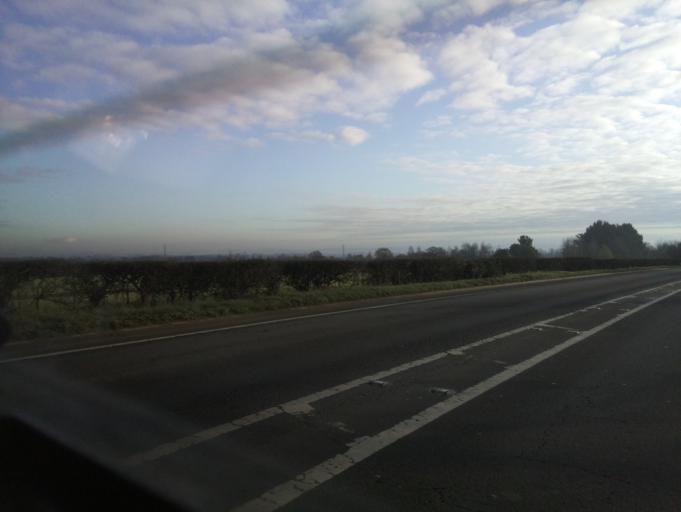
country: GB
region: England
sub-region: Warwickshire
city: Curdworth
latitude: 52.5642
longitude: -1.7466
